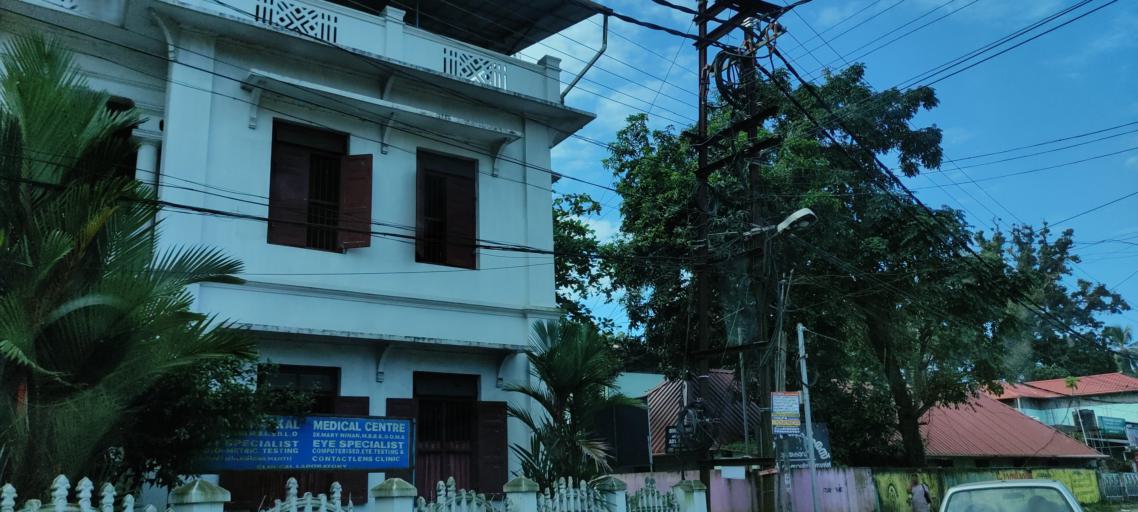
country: IN
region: Kerala
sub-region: Alappuzha
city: Mavelikara
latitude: 9.2534
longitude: 76.5454
